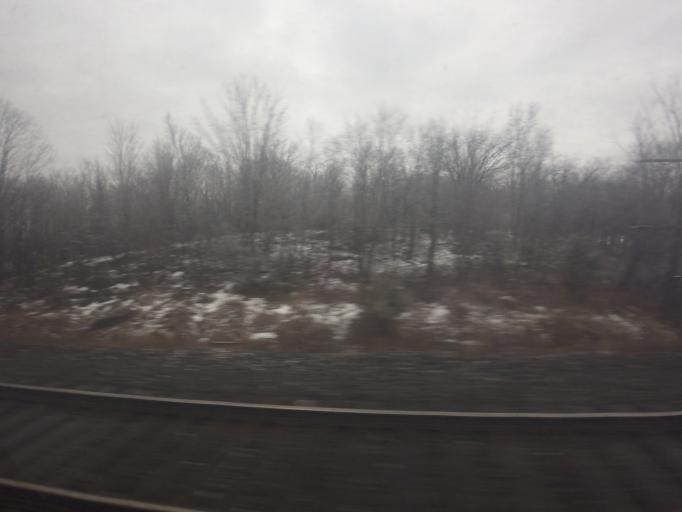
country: CA
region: Ontario
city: Gananoque
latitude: 44.3589
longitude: -76.1989
